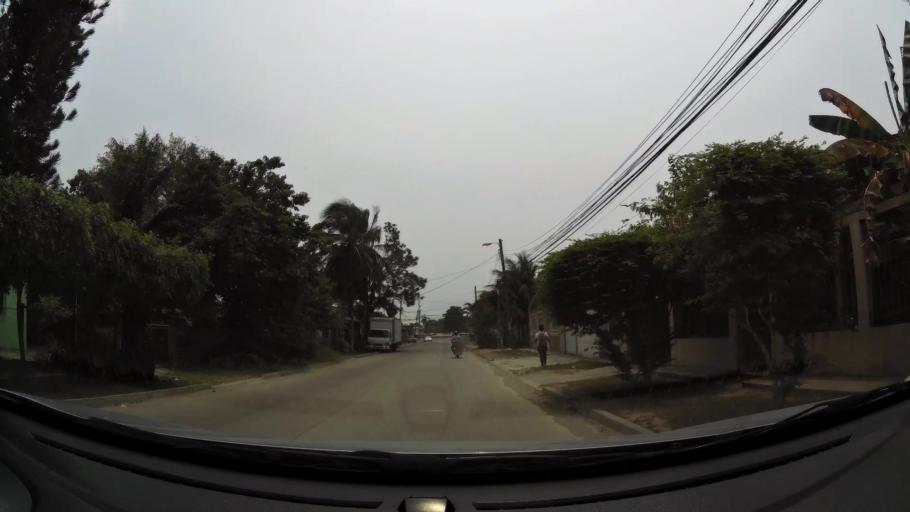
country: HN
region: Yoro
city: El Progreso
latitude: 15.3882
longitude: -87.8043
